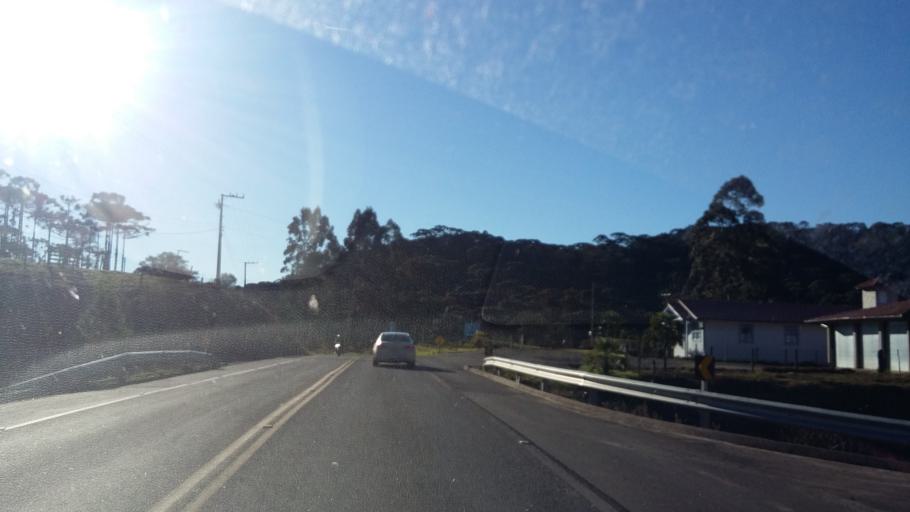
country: BR
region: Santa Catarina
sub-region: Lauro Muller
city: Lauro Muller
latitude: -28.0055
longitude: -49.5397
